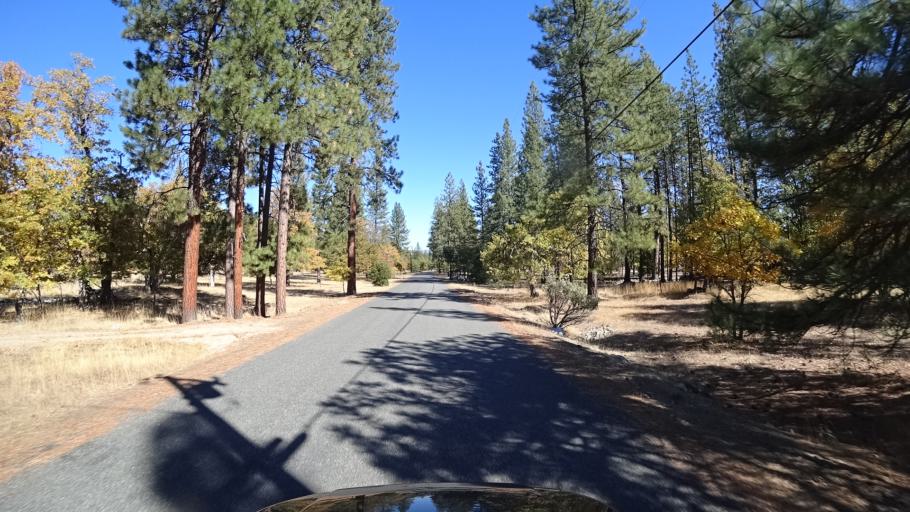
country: US
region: California
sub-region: Siskiyou County
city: Yreka
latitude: 41.5385
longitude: -122.9512
